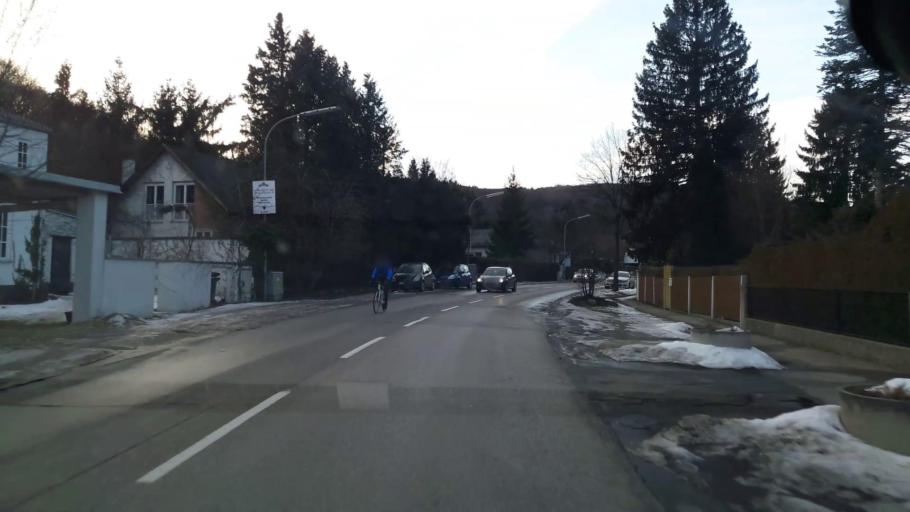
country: AT
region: Lower Austria
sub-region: Politischer Bezirk Wien-Umgebung
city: Mauerbach
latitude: 48.2350
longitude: 16.1879
